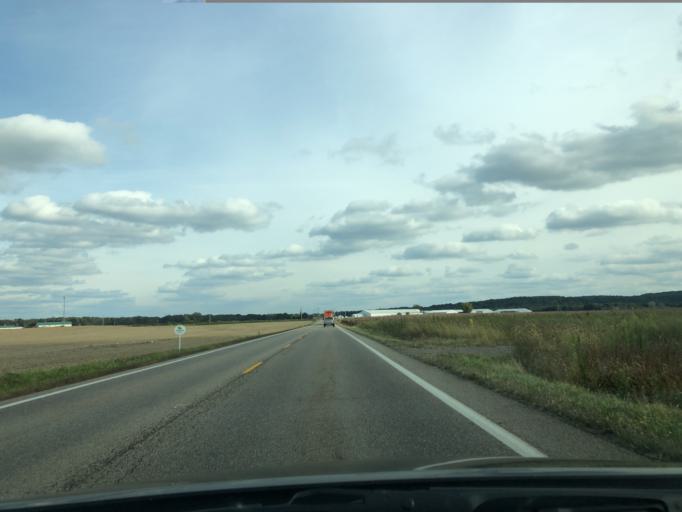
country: US
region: Ohio
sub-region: Stark County
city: Beach City
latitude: 40.6456
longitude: -81.5891
